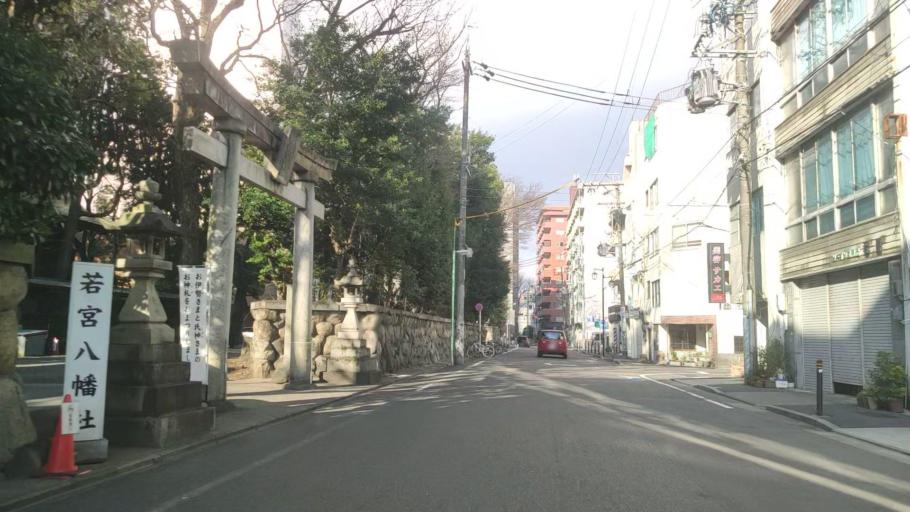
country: JP
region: Aichi
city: Nagoya-shi
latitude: 35.1637
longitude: 136.9038
